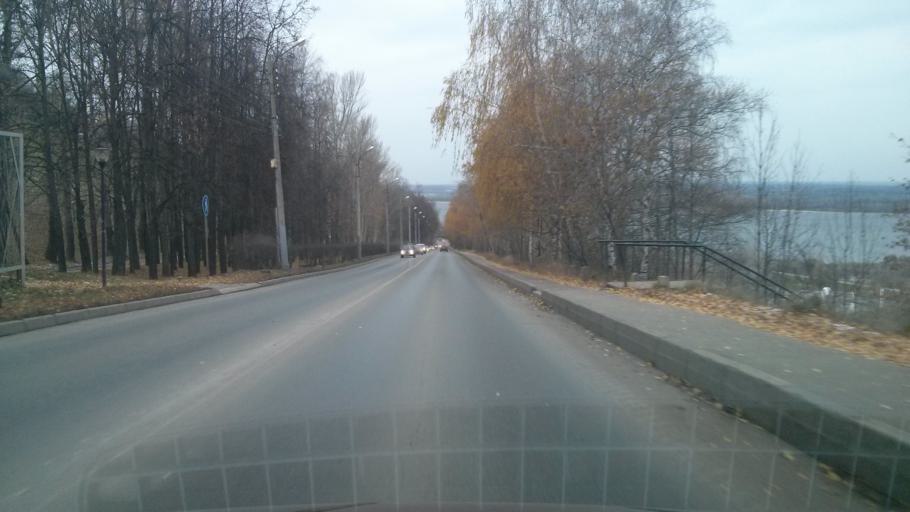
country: RU
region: Nizjnij Novgorod
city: Nizhniy Novgorod
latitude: 56.3258
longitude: 44.0337
